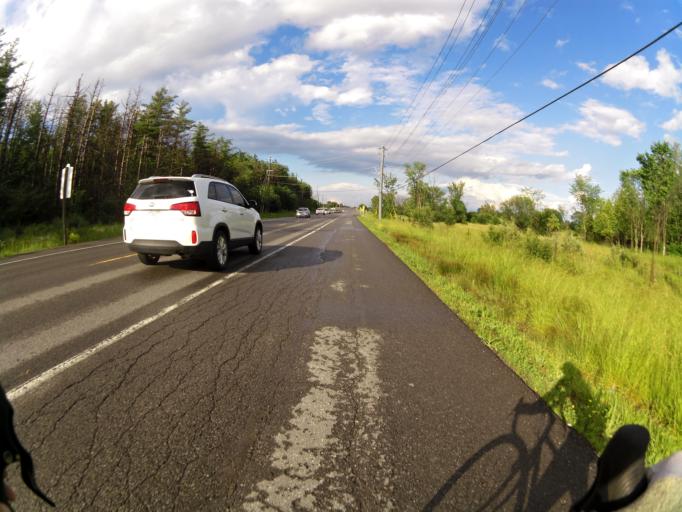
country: CA
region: Ontario
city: Bells Corners
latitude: 45.3102
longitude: -75.8086
